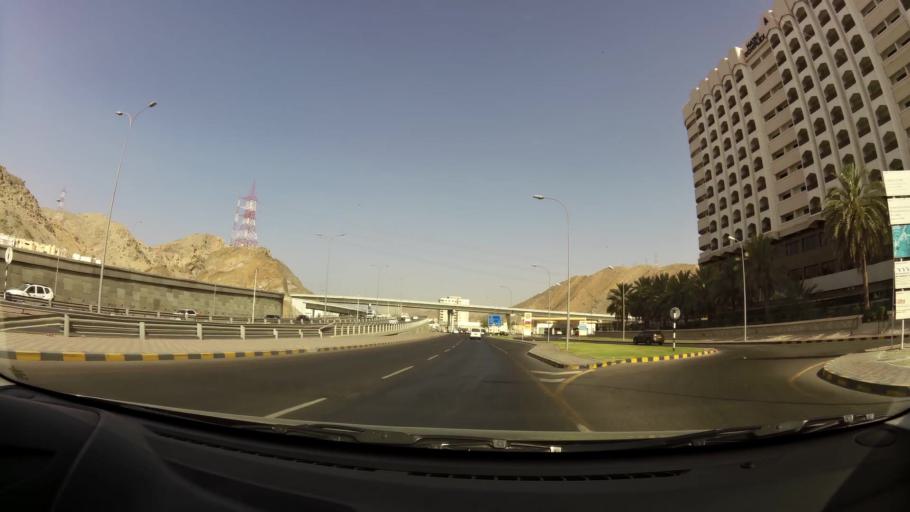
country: OM
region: Muhafazat Masqat
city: Muscat
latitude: 23.5926
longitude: 58.5238
